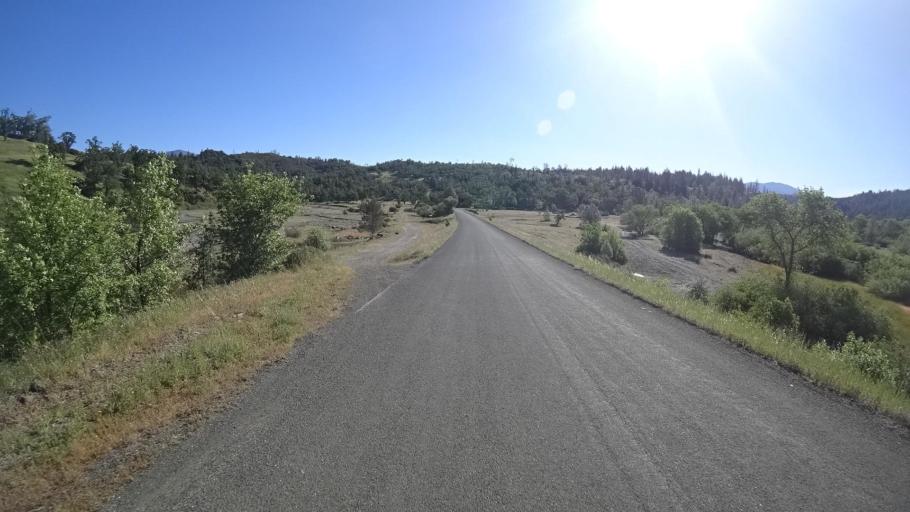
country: US
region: California
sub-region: Lake County
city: Upper Lake
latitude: 39.4109
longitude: -122.9779
